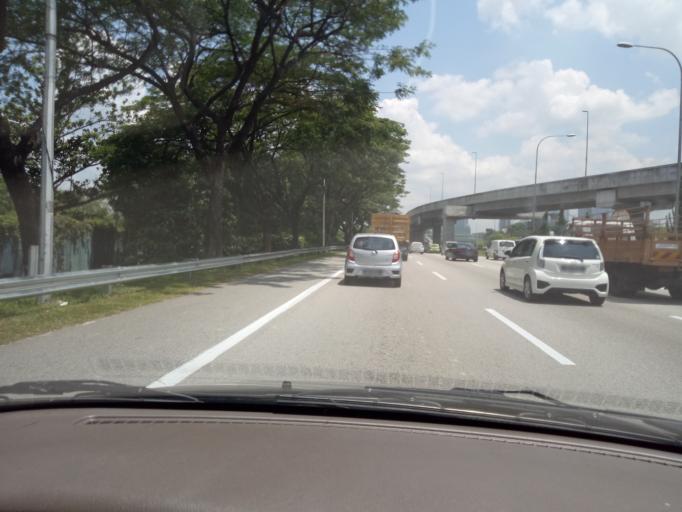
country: MY
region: Kuala Lumpur
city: Kuala Lumpur
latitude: 3.1220
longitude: 101.7072
